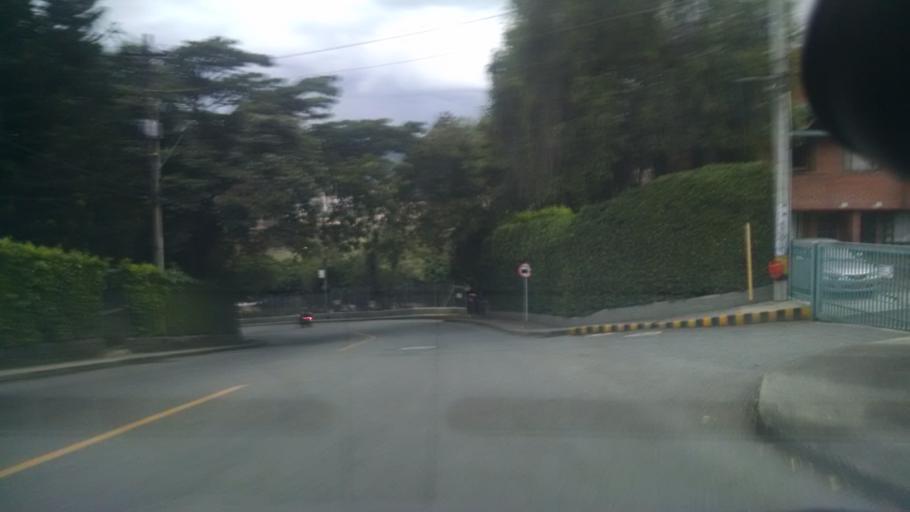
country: CO
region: Antioquia
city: Medellin
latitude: 6.2685
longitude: -75.6019
